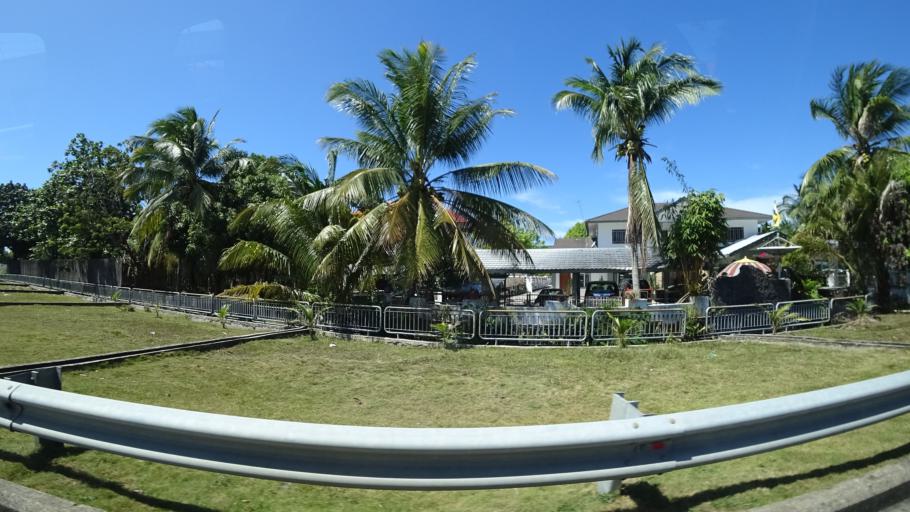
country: BN
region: Brunei and Muara
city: Bandar Seri Begawan
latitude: 4.9159
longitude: 114.9211
